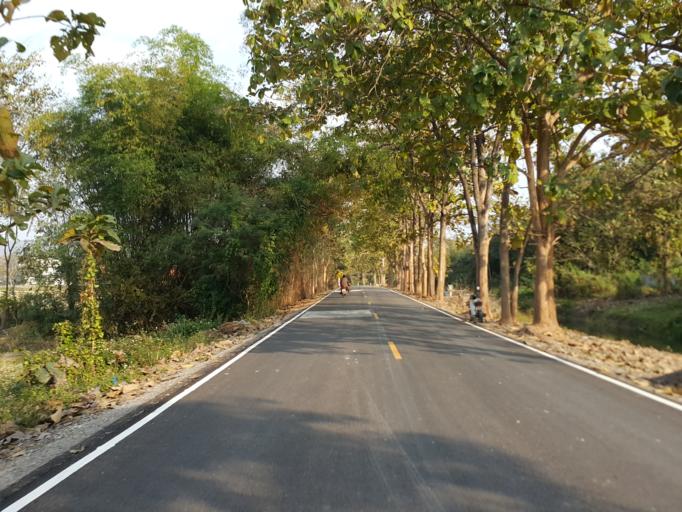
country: TH
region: Chiang Mai
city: San Sai
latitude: 18.8748
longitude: 99.1422
